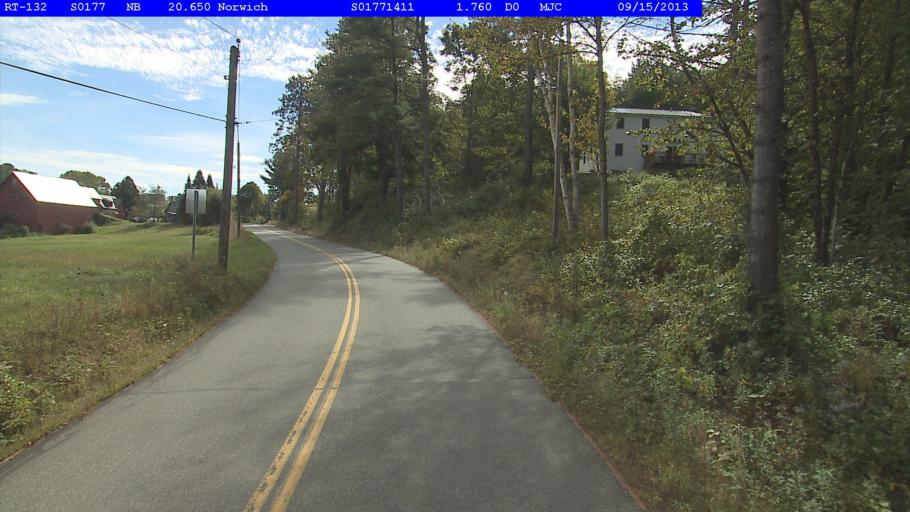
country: US
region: New Hampshire
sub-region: Grafton County
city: Hanover
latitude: 43.7660
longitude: -72.2449
